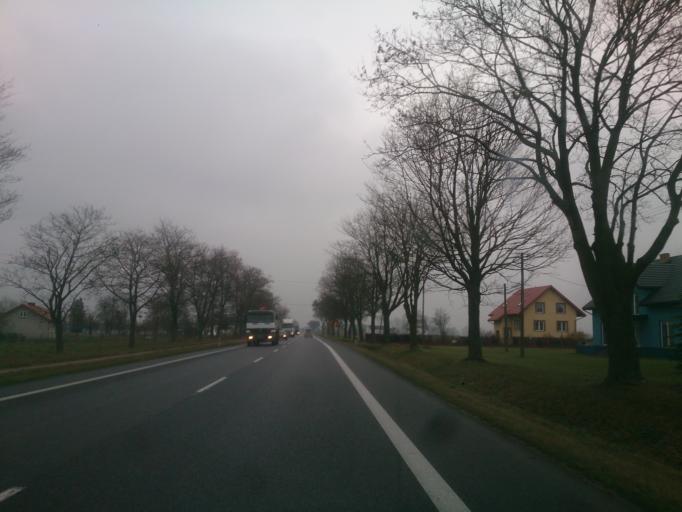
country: PL
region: Masovian Voivodeship
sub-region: Powiat sierpecki
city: Zawidz
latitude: 52.8131
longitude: 19.8049
